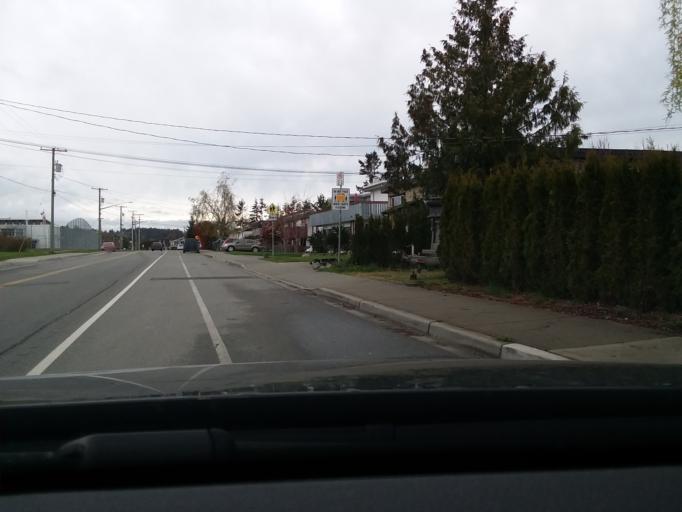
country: CA
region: British Columbia
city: North Saanich
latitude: 48.6640
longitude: -123.4169
